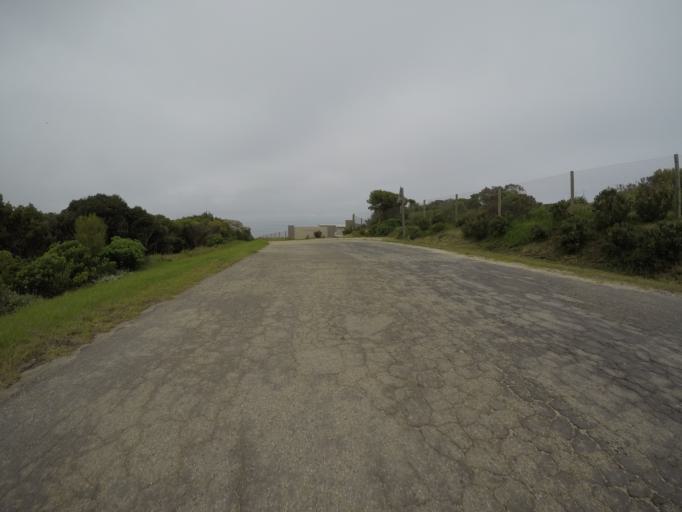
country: ZA
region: Eastern Cape
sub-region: Cacadu District Municipality
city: Kareedouw
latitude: -34.0732
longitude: 24.2325
